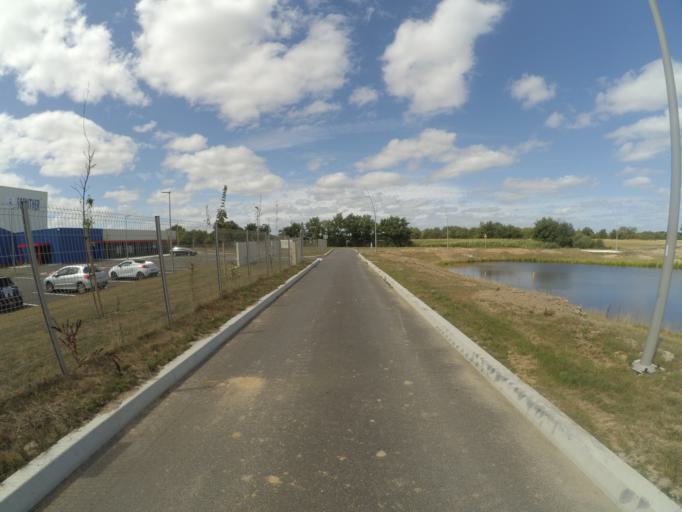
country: FR
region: Pays de la Loire
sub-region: Departement de la Vendee
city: Saint-Hilaire-de-Loulay
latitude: 47.0255
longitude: -1.3539
